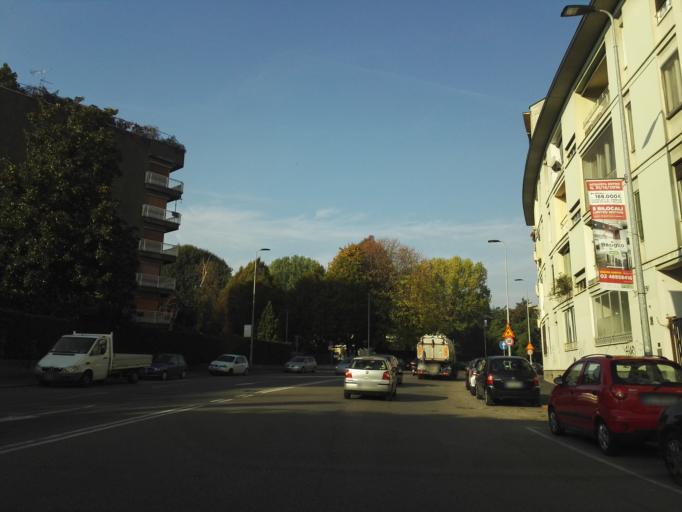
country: IT
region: Lombardy
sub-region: Citta metropolitana di Milano
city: Milano
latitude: 45.4361
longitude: 9.2003
